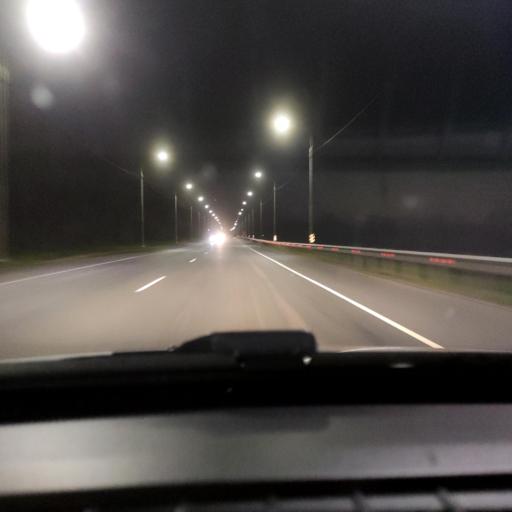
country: RU
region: Voronezj
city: Kashirskoye
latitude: 51.4987
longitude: 39.5862
